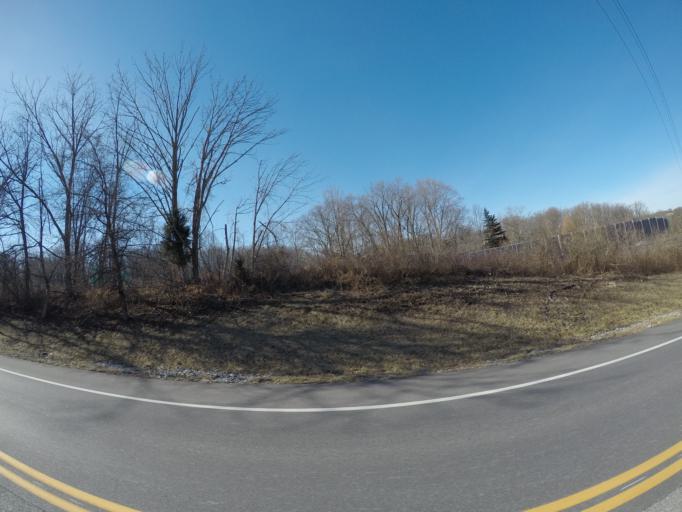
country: US
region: Maryland
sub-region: Howard County
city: Ellicott City
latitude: 39.2685
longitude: -76.8179
